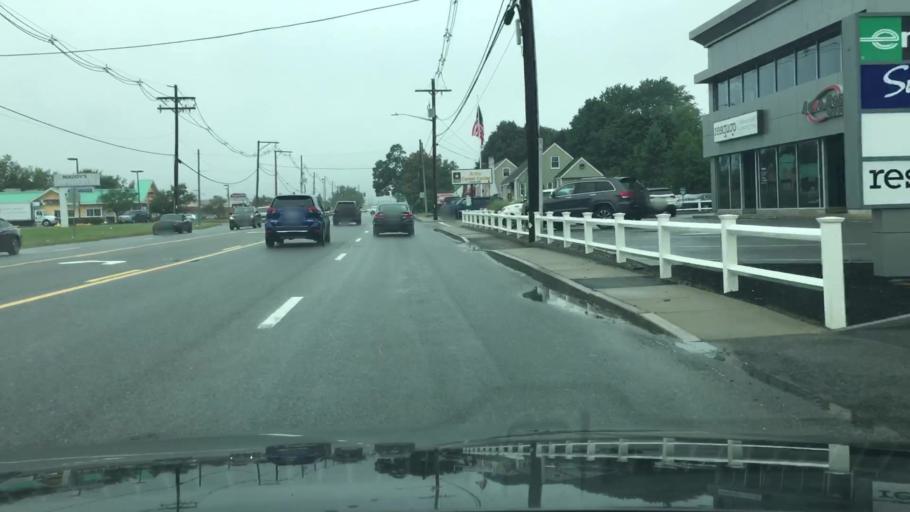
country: US
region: Massachusetts
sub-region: Essex County
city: Peabody
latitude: 42.5491
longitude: -70.9525
